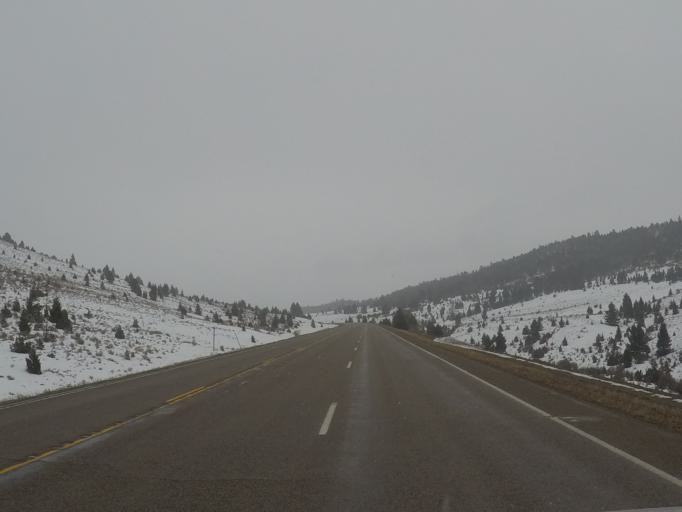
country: US
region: Montana
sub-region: Meagher County
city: White Sulphur Springs
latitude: 46.6542
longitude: -110.8720
